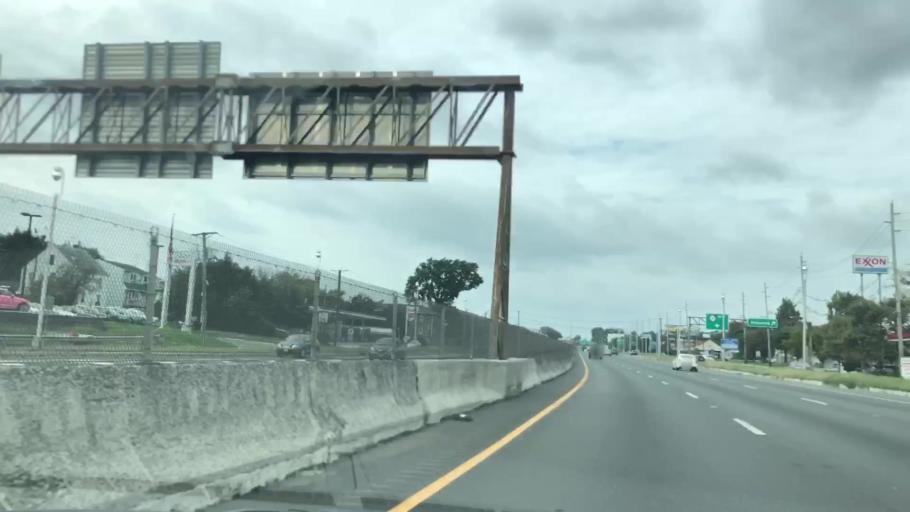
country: US
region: New Jersey
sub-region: Hudson County
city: Secaucus
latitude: 40.7892
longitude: -74.0513
